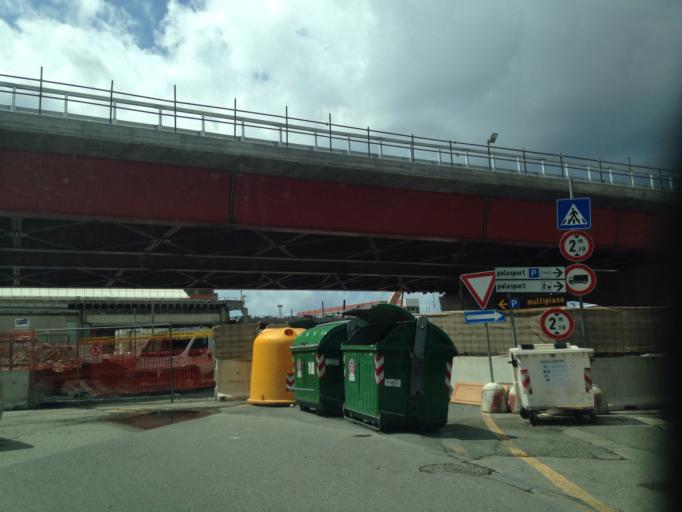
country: IT
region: Liguria
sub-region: Provincia di Genova
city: San Teodoro
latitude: 44.4118
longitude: 8.8805
